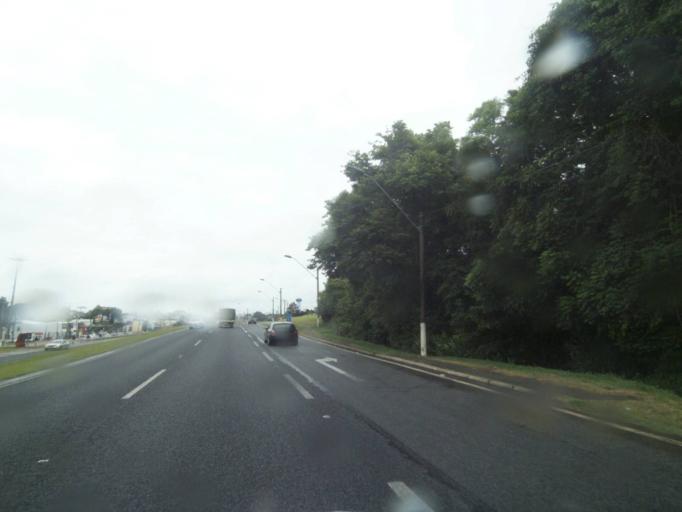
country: BR
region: Parana
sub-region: Curitiba
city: Curitiba
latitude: -25.4305
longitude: -49.3407
